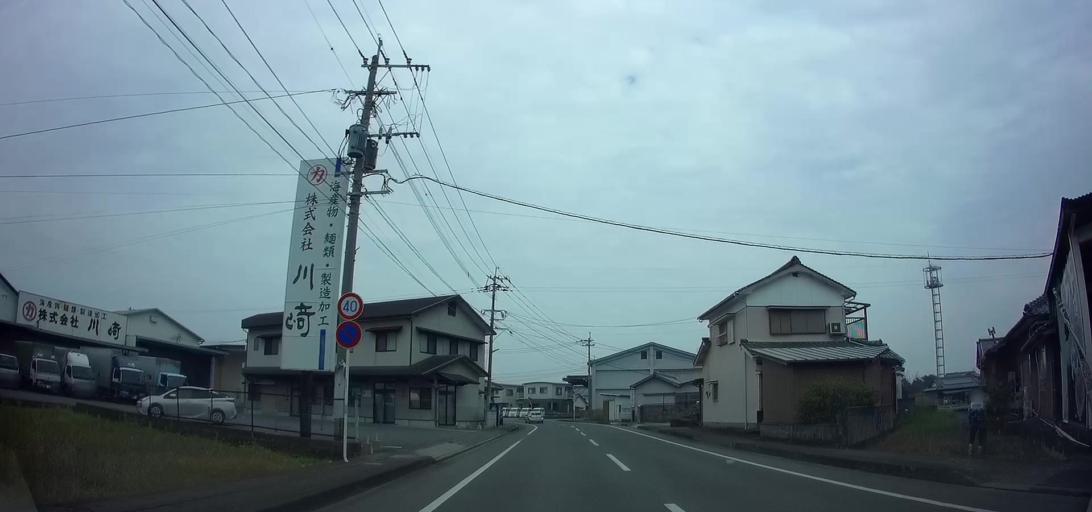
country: JP
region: Nagasaki
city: Shimabara
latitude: 32.6530
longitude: 130.2981
